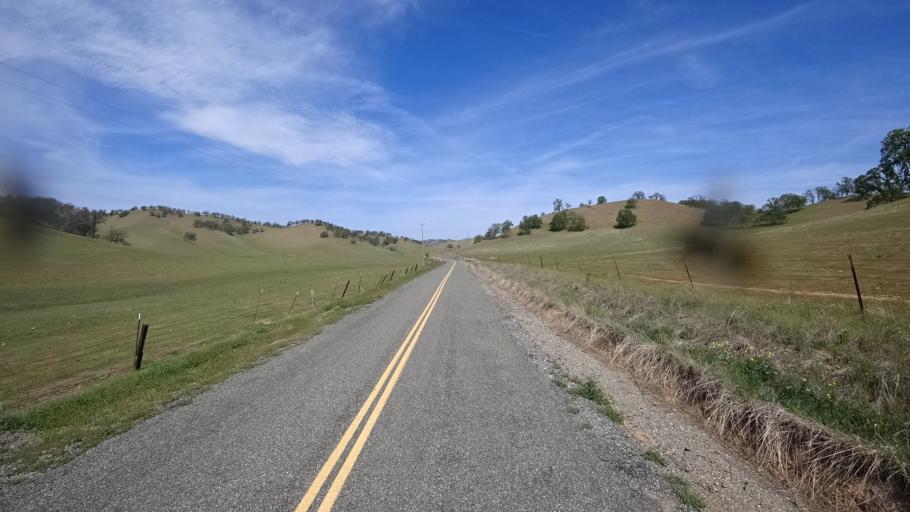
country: US
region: California
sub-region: Glenn County
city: Willows
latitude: 39.5793
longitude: -122.4466
